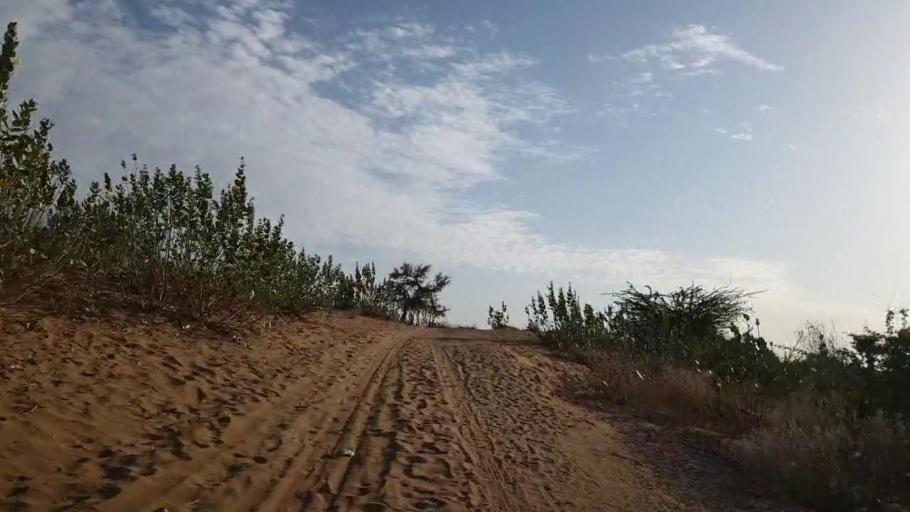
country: PK
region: Sindh
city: Nabisar
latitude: 25.0815
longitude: 69.9894
